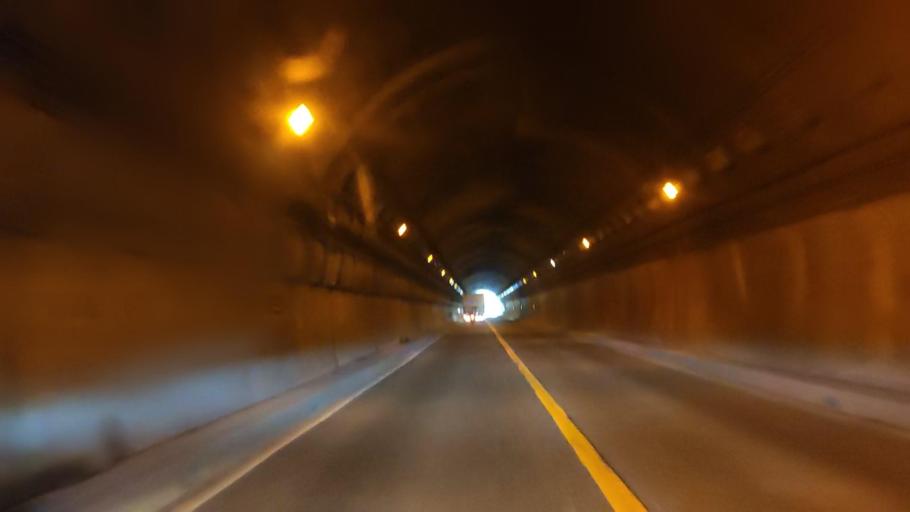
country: JP
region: Shizuoka
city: Fujinomiya
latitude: 35.2075
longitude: 138.5160
